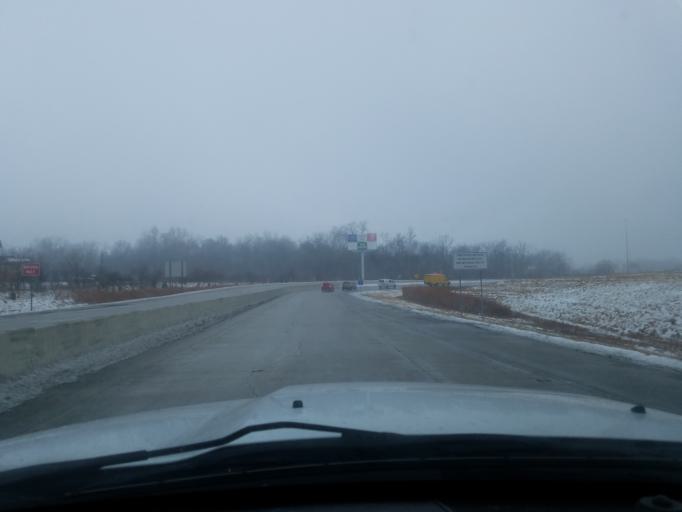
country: US
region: Indiana
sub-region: Marion County
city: Warren Park
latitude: 39.7508
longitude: -86.0321
